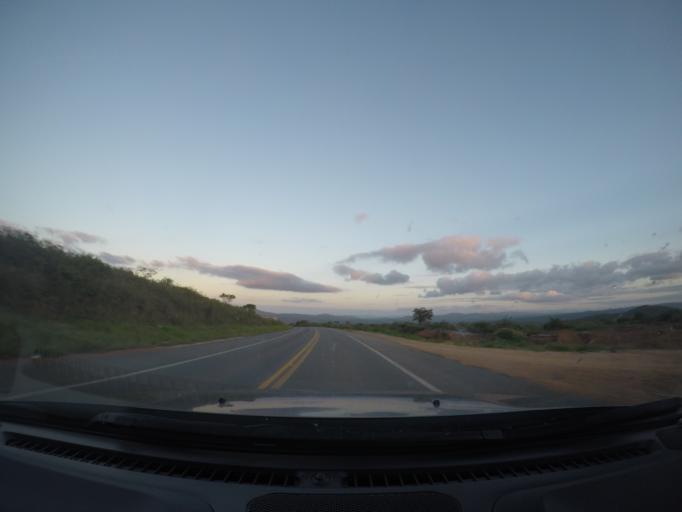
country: BR
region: Bahia
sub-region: Seabra
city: Seabra
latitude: -12.4339
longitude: -41.8213
